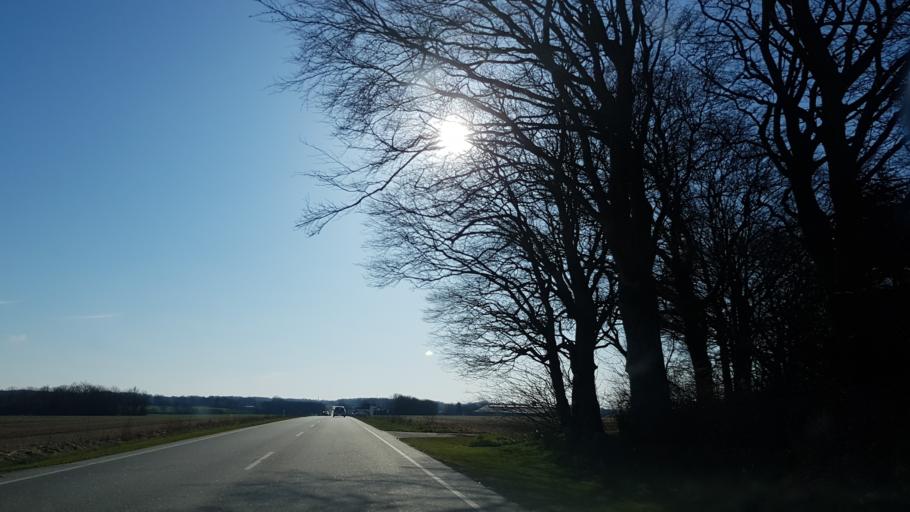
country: DK
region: South Denmark
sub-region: Vejen Kommune
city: Rodding
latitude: 55.3995
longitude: 9.1078
